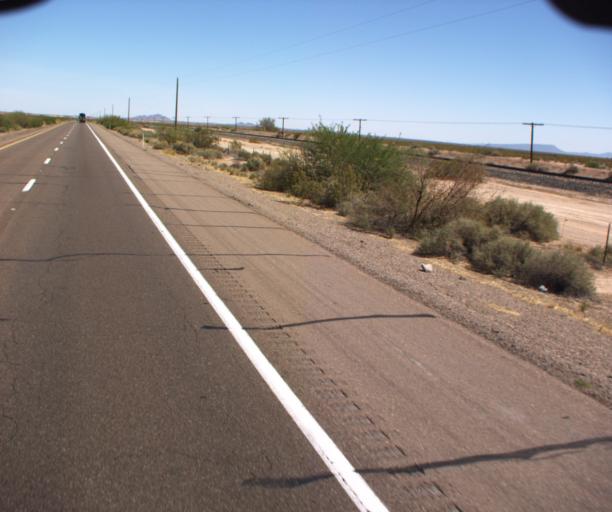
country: US
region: Arizona
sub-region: Yuma County
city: Wellton
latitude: 32.7422
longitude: -113.6832
